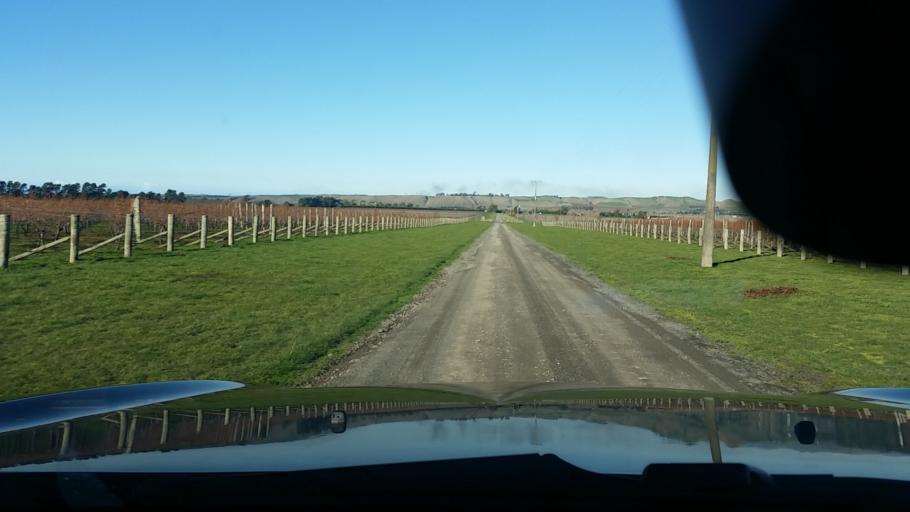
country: NZ
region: Marlborough
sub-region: Marlborough District
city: Blenheim
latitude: -41.6407
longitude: 174.0377
